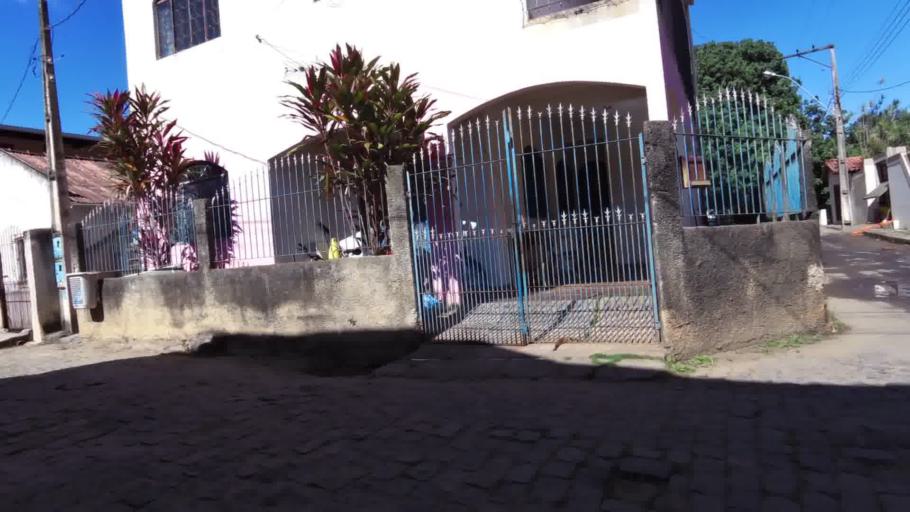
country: BR
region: Espirito Santo
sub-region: Rio Novo Do Sul
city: Rio Novo do Sul
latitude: -20.8627
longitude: -40.9337
